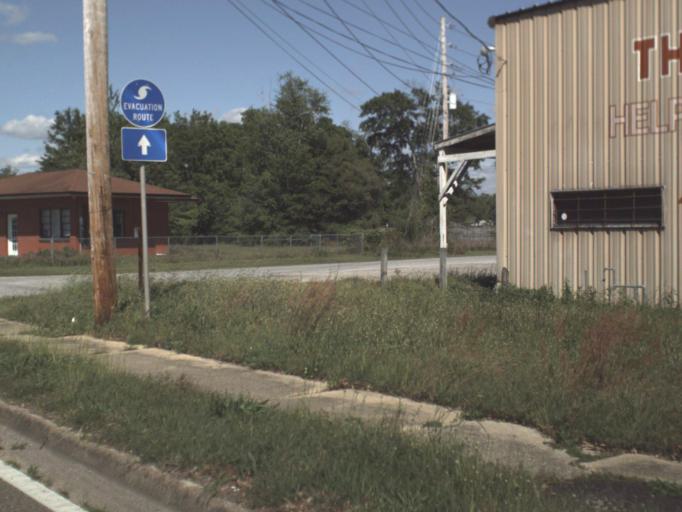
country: US
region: Florida
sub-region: Escambia County
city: Ferry Pass
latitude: 30.5316
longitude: -87.2071
